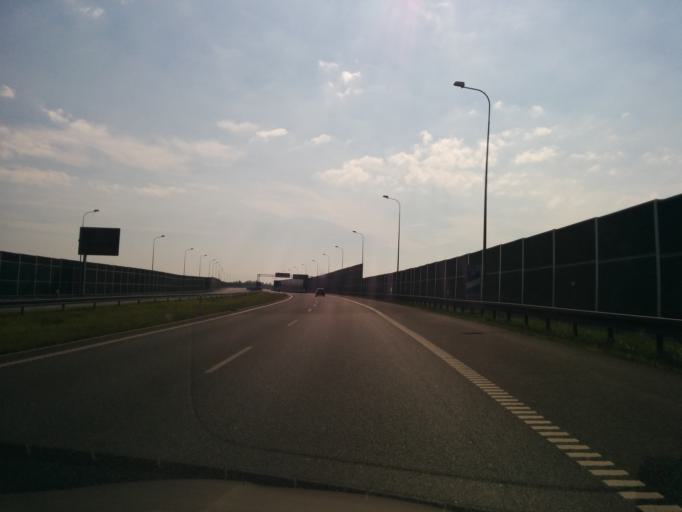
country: PL
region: Silesian Voivodeship
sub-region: Powiat tarnogorski
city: Radzionkow
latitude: 50.3725
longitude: 18.8874
